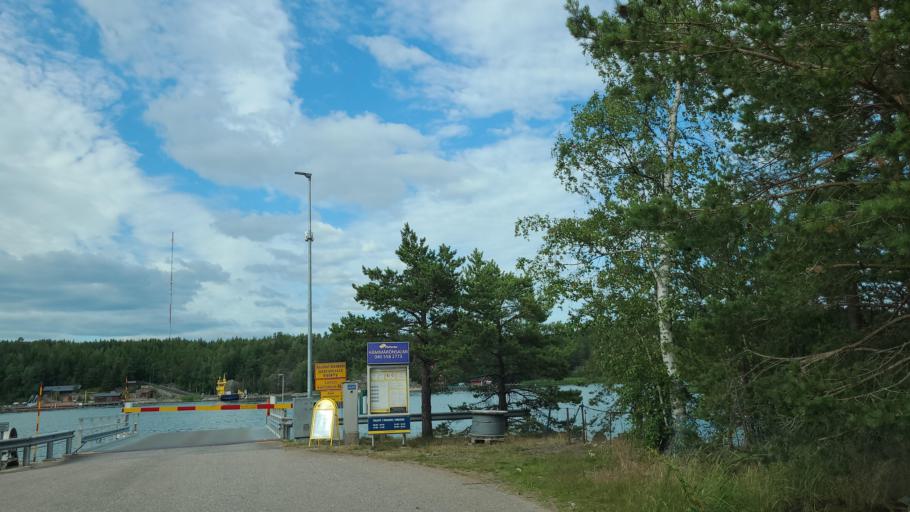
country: FI
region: Varsinais-Suomi
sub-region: Turku
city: Rymaettylae
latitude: 60.3135
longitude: 21.9613
